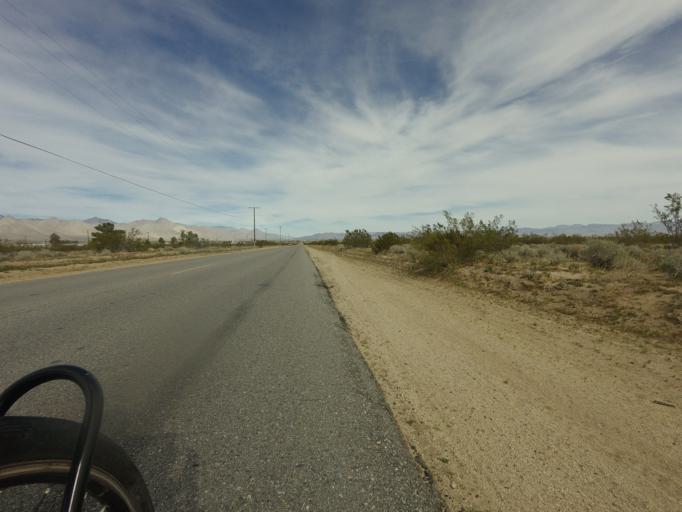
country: US
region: California
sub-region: Kern County
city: Inyokern
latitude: 35.6935
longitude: -117.8261
